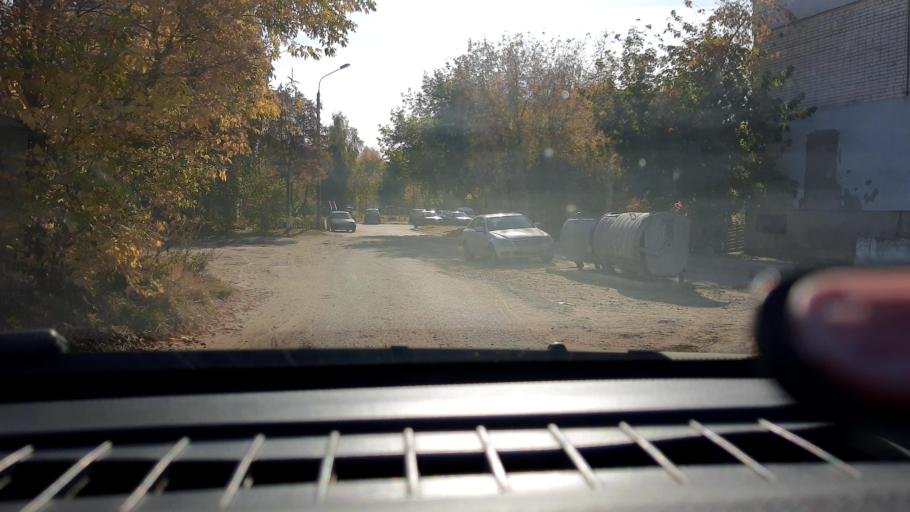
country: RU
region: Nizjnij Novgorod
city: Burevestnik
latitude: 56.2035
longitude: 43.8100
